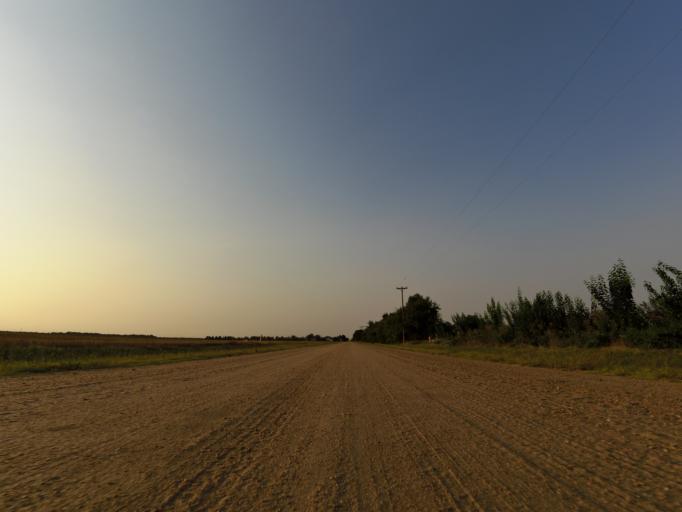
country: US
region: Kansas
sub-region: Reno County
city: South Hutchinson
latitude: 37.9996
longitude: -97.9955
